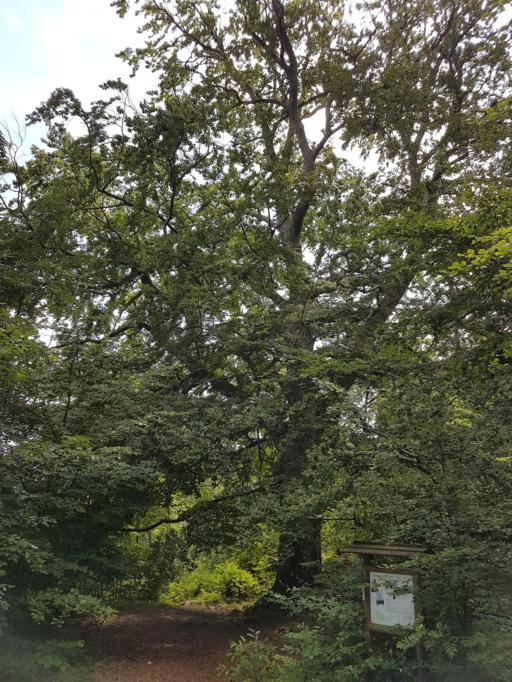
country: IT
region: Veneto
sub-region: Provincia di Vicenza
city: Recoaro Terme
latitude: 45.6776
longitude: 11.2002
